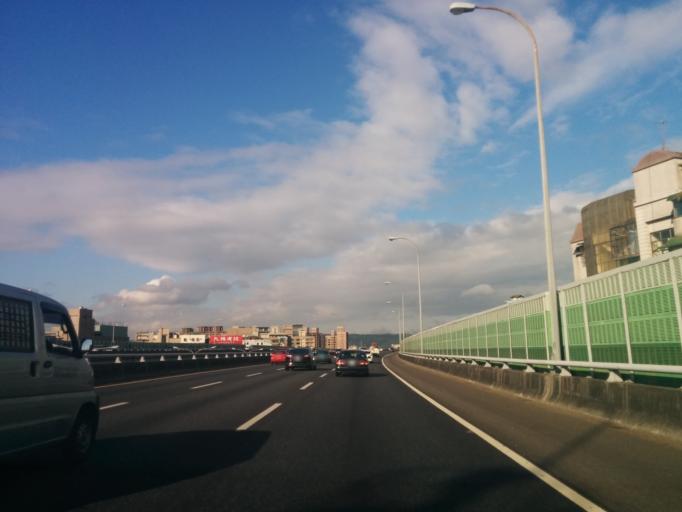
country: TW
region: Taipei
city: Taipei
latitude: 25.0738
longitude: 121.4788
